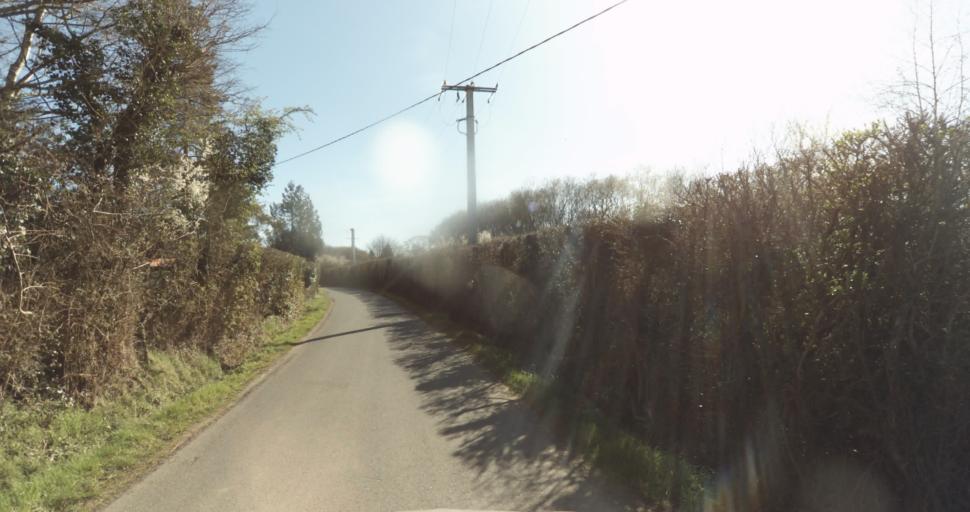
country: FR
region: Lower Normandy
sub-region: Departement du Calvados
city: Saint-Pierre-sur-Dives
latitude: 49.0287
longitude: 0.0561
